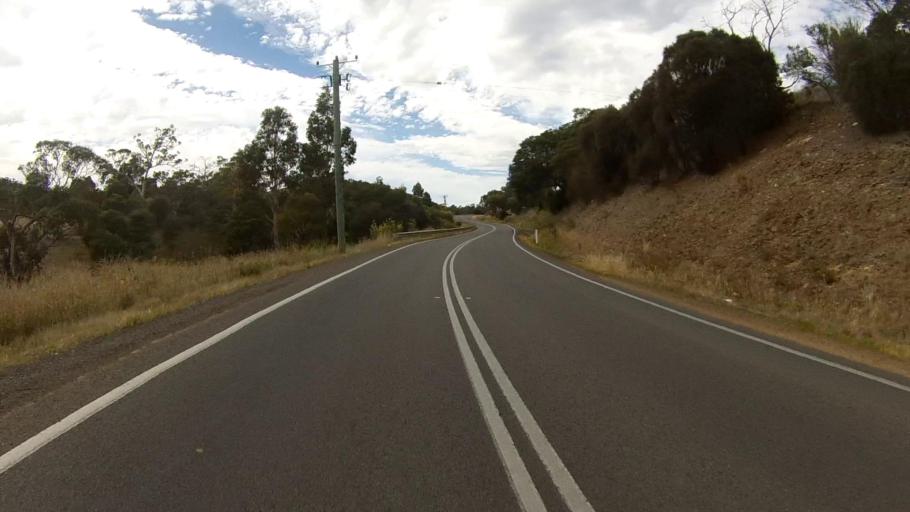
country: AU
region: Tasmania
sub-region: Sorell
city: Sorell
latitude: -42.6960
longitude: 147.4796
